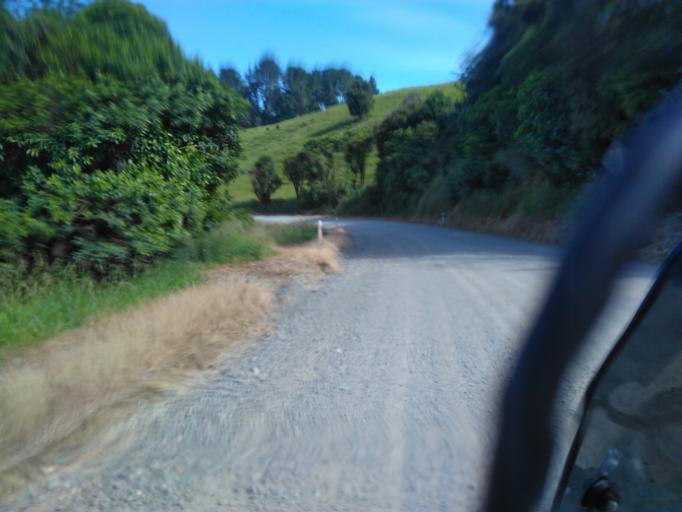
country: NZ
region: Hawke's Bay
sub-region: Wairoa District
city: Wairoa
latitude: -38.8702
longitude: 177.2067
